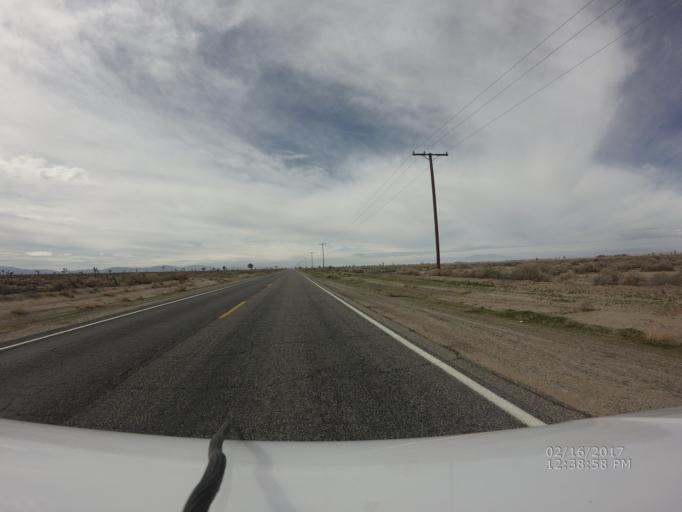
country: US
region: California
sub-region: Los Angeles County
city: Lake Los Angeles
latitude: 34.6754
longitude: -117.8892
